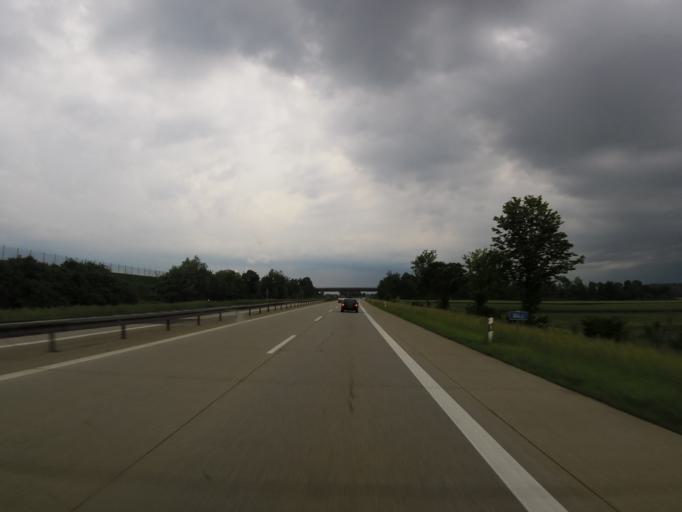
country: DE
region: Bavaria
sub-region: Lower Bavaria
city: Niederviehbach
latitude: 48.6377
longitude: 12.3798
